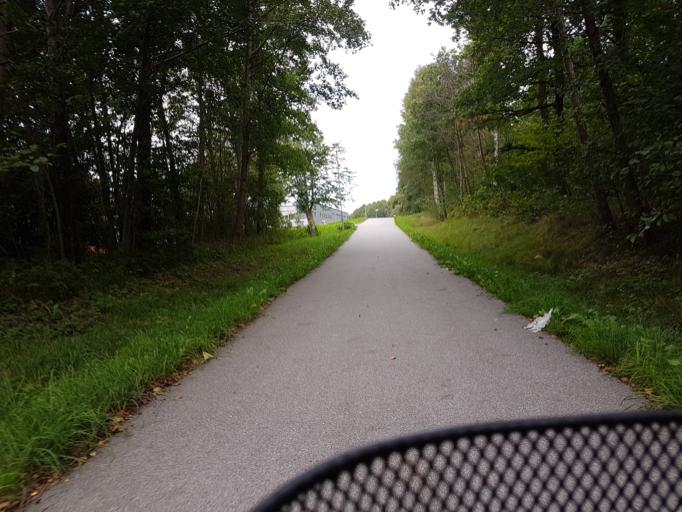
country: SE
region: Vaestra Goetaland
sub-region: Ale Kommun
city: Nodinge-Nol
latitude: 57.8988
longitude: 12.0576
